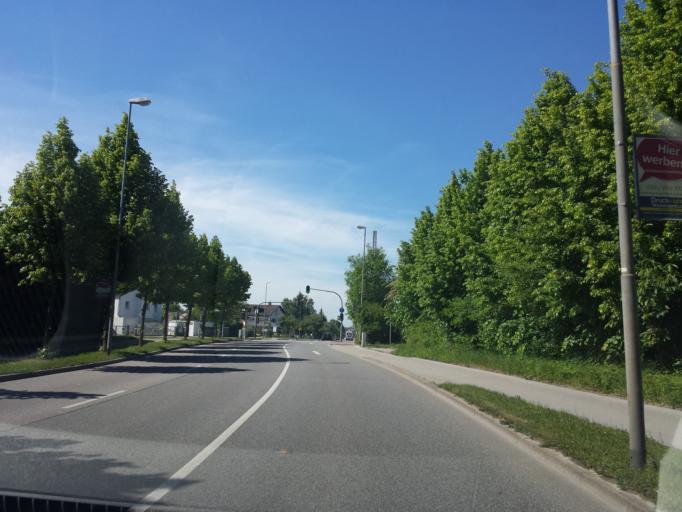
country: DE
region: Bavaria
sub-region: Upper Bavaria
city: Ingolstadt
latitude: 48.7311
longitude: 11.4422
